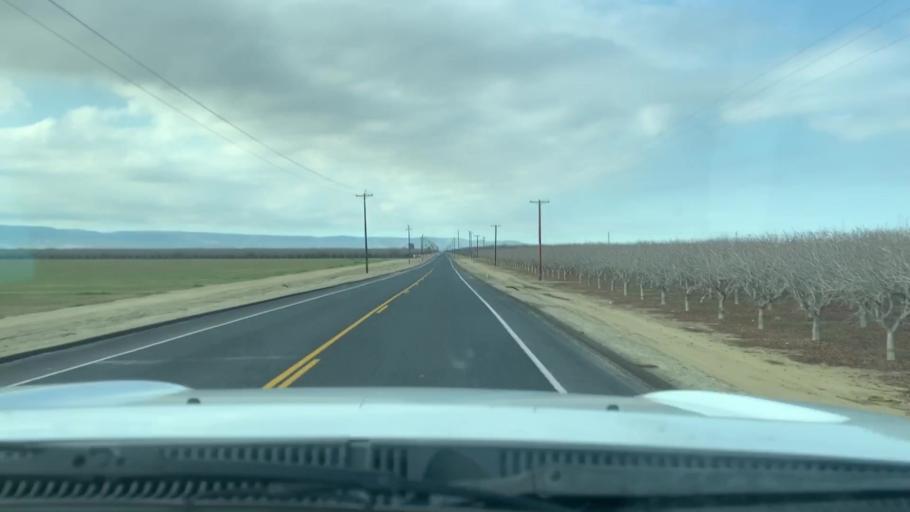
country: US
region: California
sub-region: Kern County
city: Lost Hills
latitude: 35.4993
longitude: -119.6500
